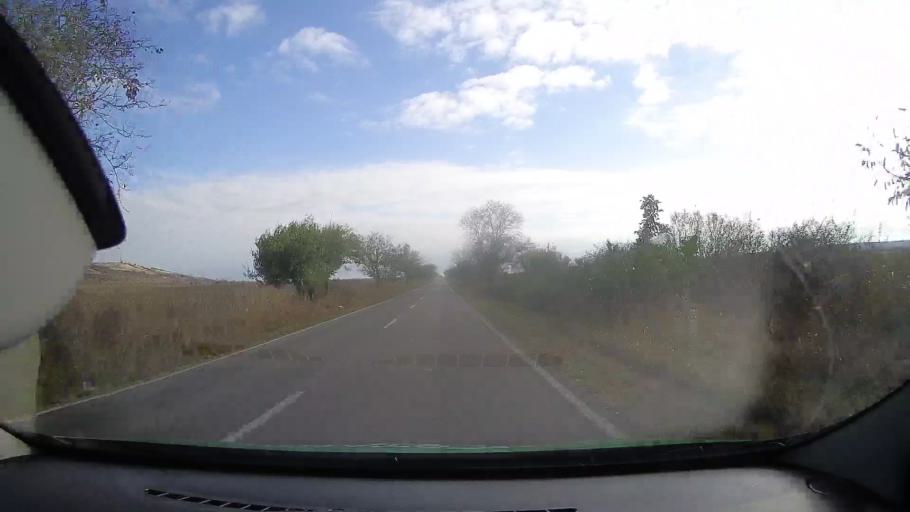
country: RO
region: Tulcea
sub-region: Comuna Mahmudia
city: Mahmudia
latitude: 45.0778
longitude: 29.0541
